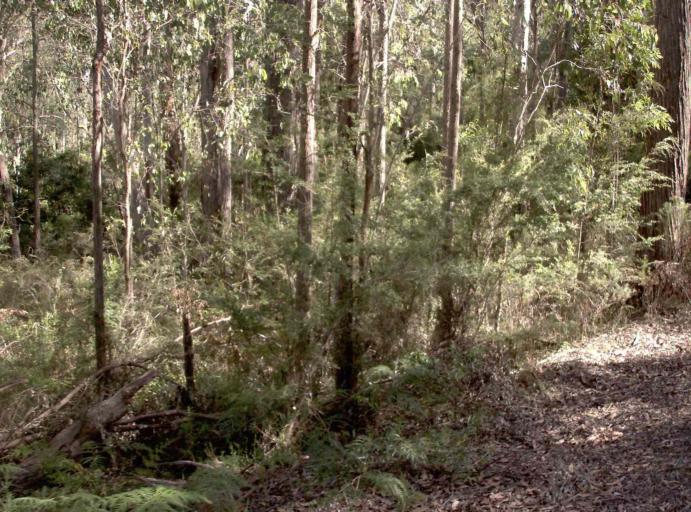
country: AU
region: Victoria
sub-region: East Gippsland
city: Lakes Entrance
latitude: -37.4585
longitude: 148.5698
